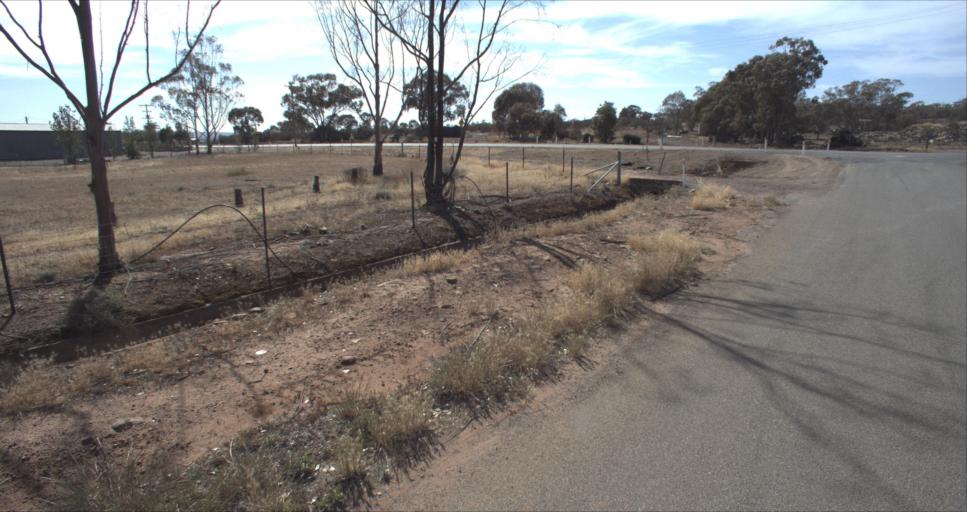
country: AU
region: New South Wales
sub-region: Leeton
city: Leeton
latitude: -34.5779
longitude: 146.4782
